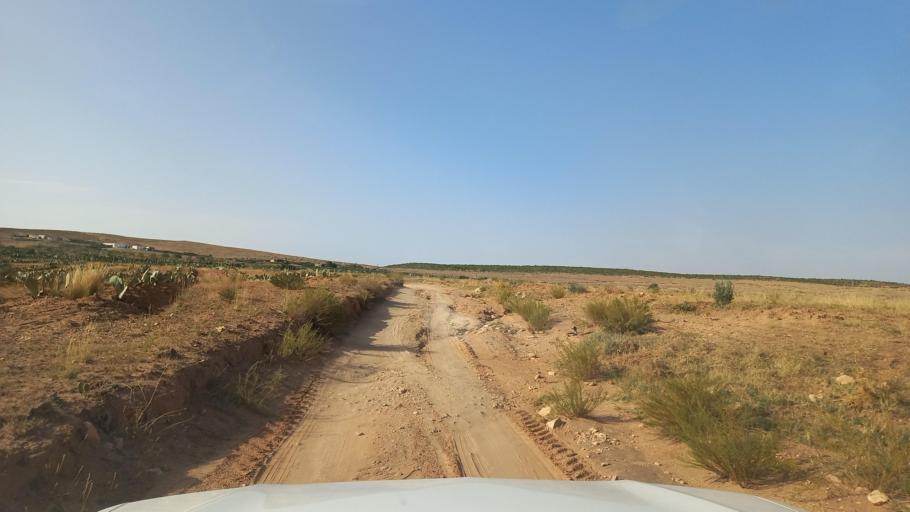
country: TN
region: Al Qasrayn
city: Kasserine
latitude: 35.3578
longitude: 8.8529
